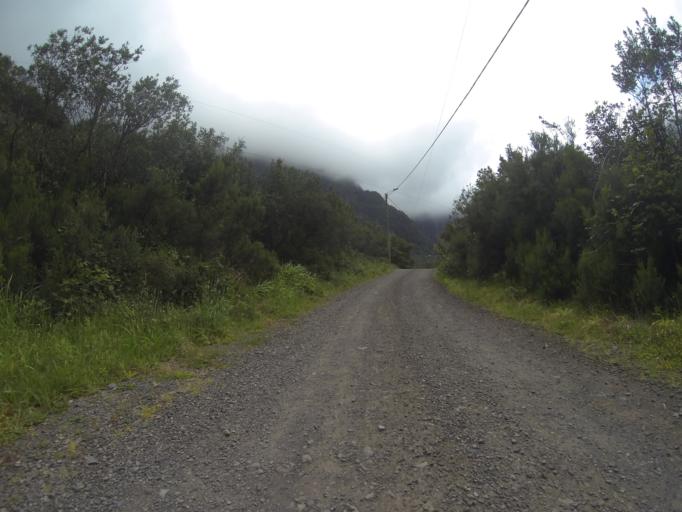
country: PT
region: Madeira
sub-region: Porto Moniz
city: Porto Moniz
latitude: 32.8010
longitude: -17.1153
